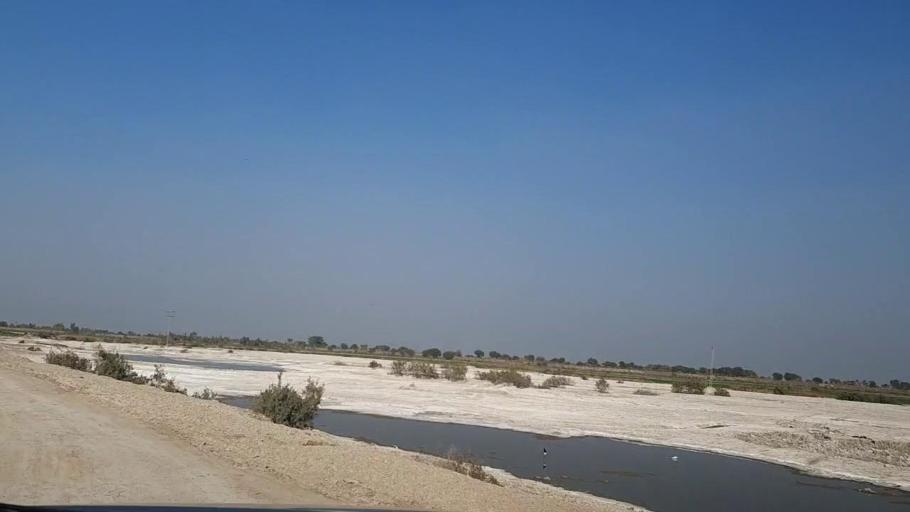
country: PK
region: Sindh
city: Daur
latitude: 26.3178
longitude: 68.1911
